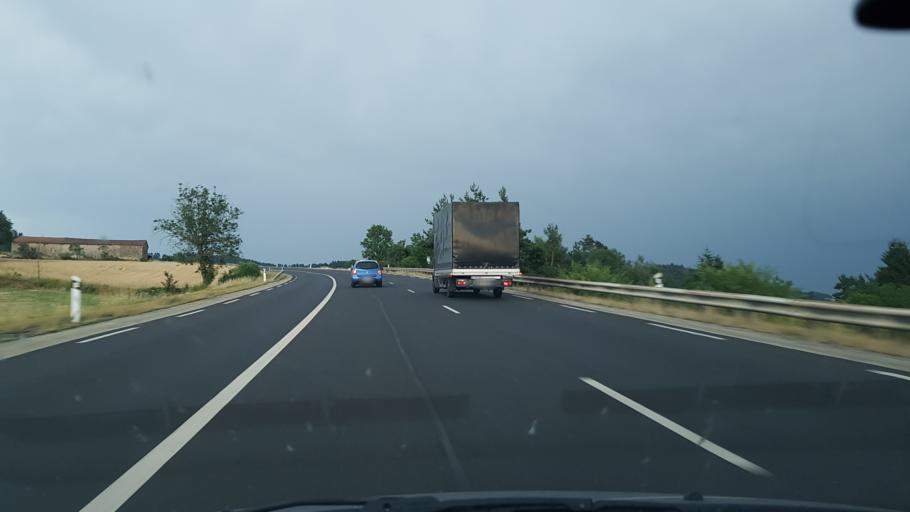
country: FR
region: Auvergne
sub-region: Departement de la Haute-Loire
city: Allegre
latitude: 45.1366
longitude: 3.6356
